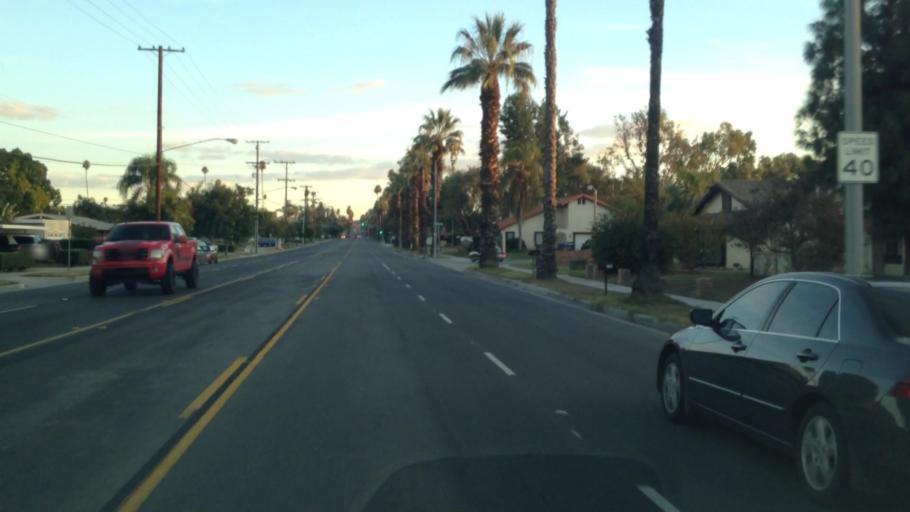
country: US
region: California
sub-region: Riverside County
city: Riverside
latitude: 33.9302
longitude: -117.4437
